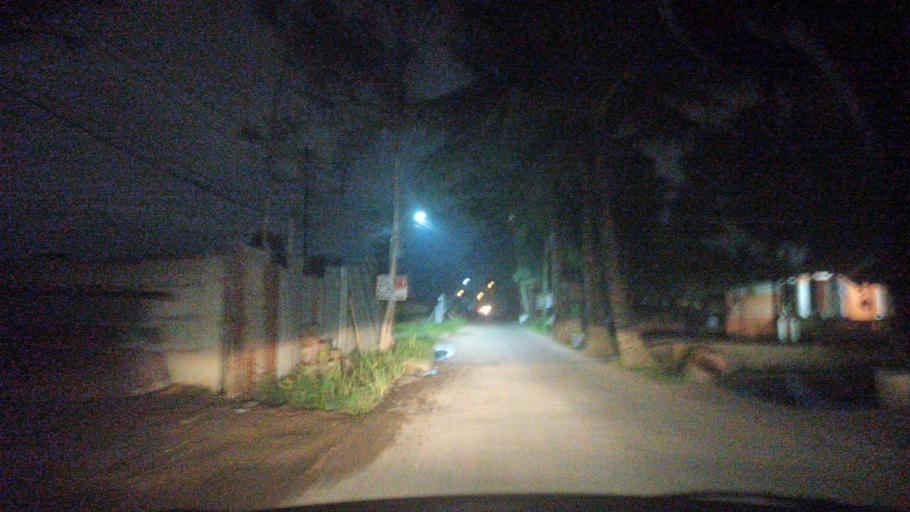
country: ID
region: South Sumatra
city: Palembang
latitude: -2.9226
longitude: 104.8009
